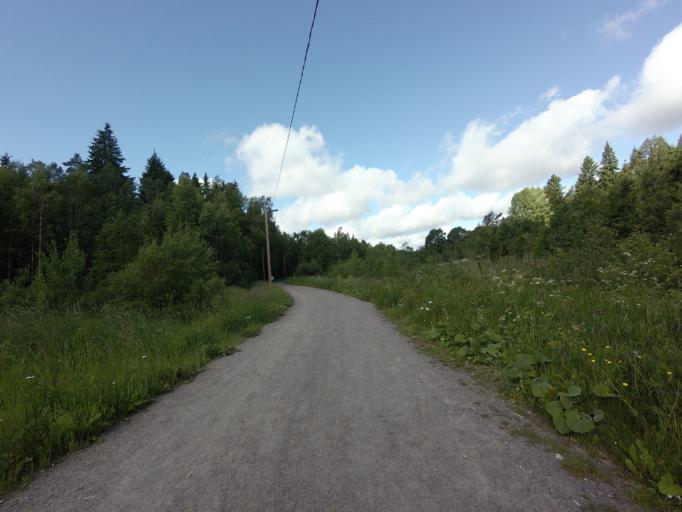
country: FI
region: Uusimaa
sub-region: Helsinki
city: Espoo
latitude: 60.1844
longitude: 24.6349
